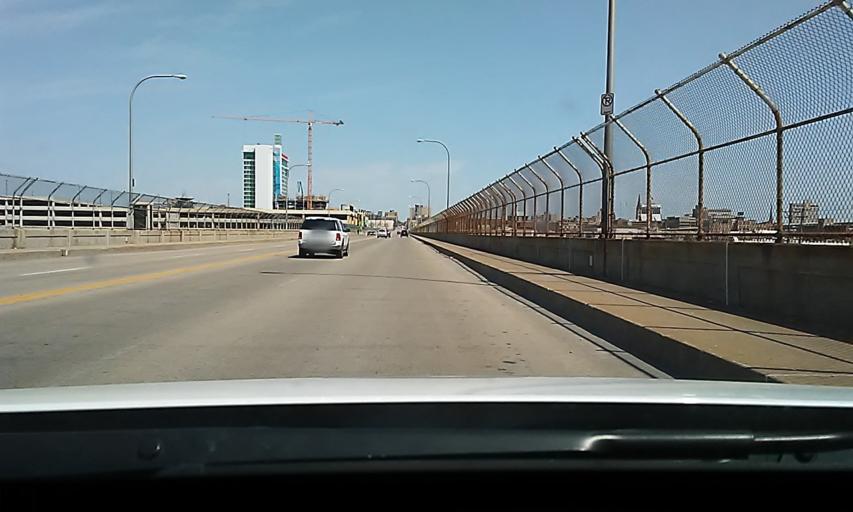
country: US
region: Wisconsin
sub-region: Milwaukee County
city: Milwaukee
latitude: 43.0258
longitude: -87.9329
